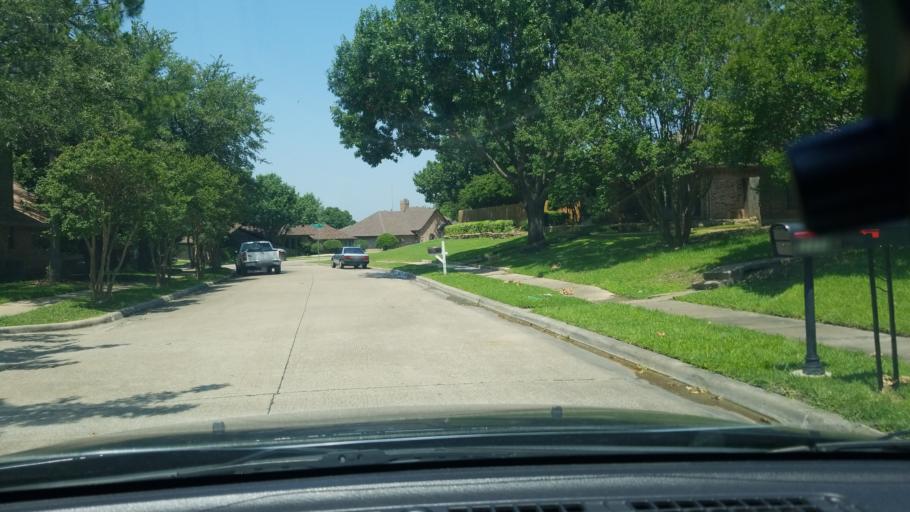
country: US
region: Texas
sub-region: Dallas County
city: Sunnyvale
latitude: 32.8266
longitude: -96.6130
